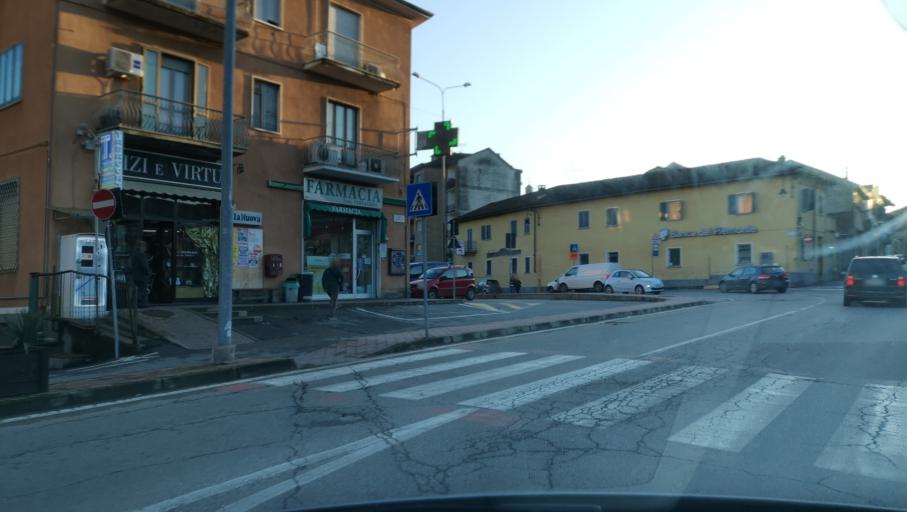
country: IT
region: Piedmont
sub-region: Provincia di Torino
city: Gassino Torinese
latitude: 45.1305
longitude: 7.8256
